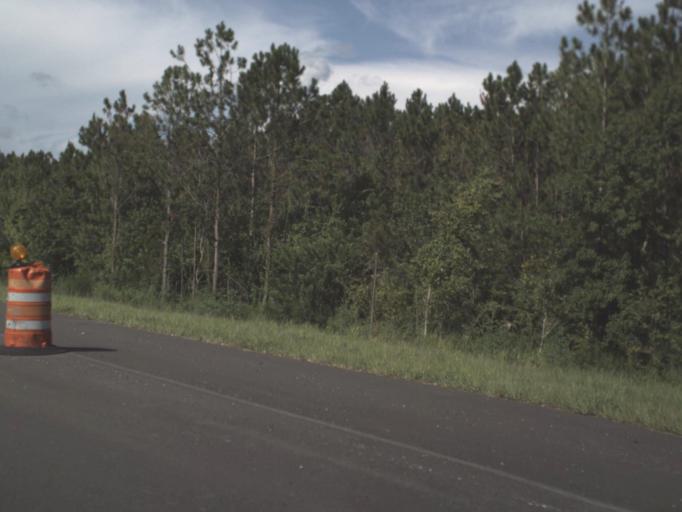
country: US
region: Florida
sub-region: Hillsborough County
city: Pebble Creek
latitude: 28.1698
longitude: -82.3946
